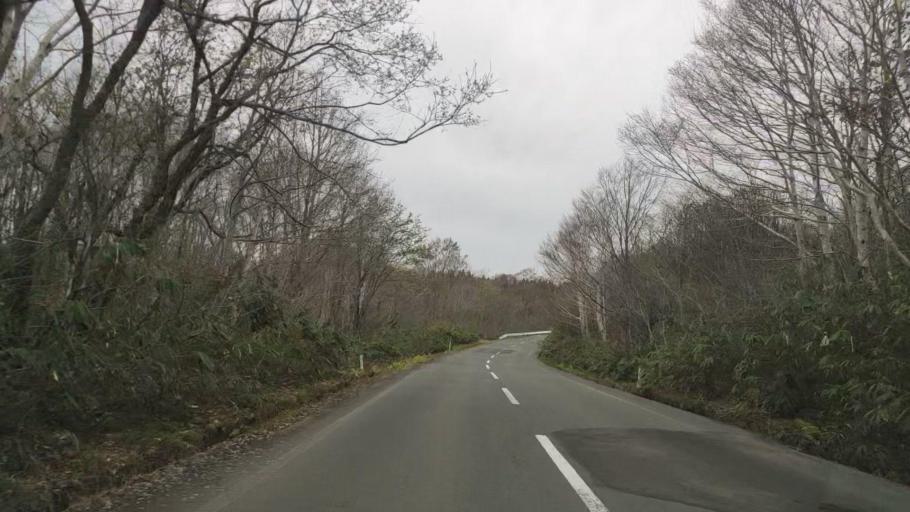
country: JP
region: Akita
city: Hanawa
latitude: 40.4083
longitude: 140.8505
